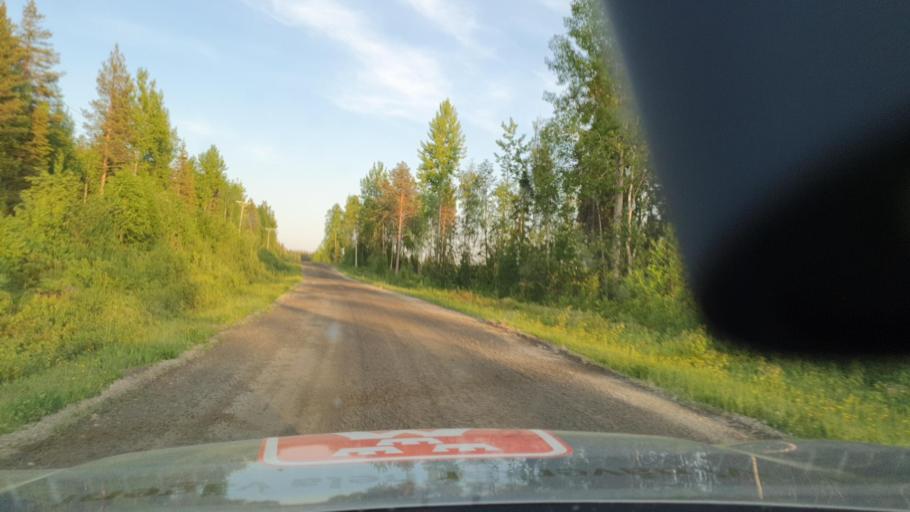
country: SE
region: Norrbotten
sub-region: Bodens Kommun
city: Boden
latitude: 66.1146
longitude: 21.5592
